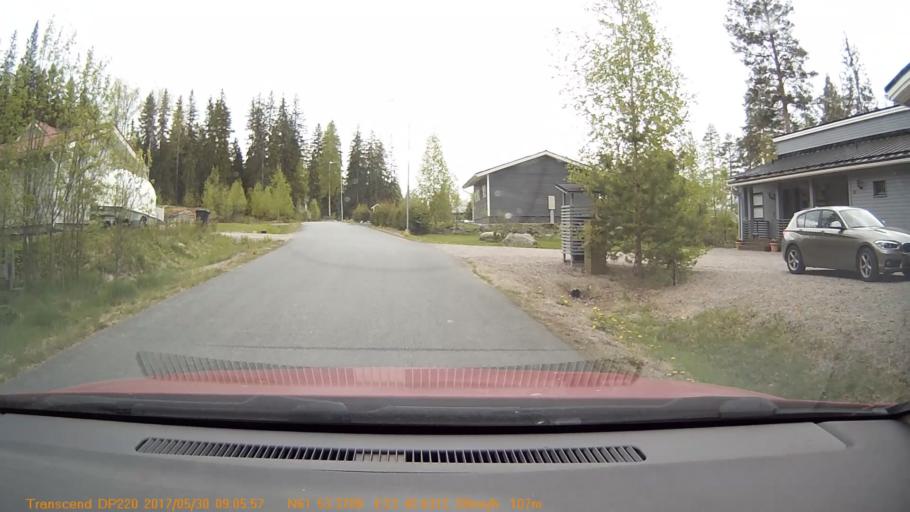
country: FI
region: Pirkanmaa
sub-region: Tampere
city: Kuru
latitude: 61.8893
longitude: 23.7111
